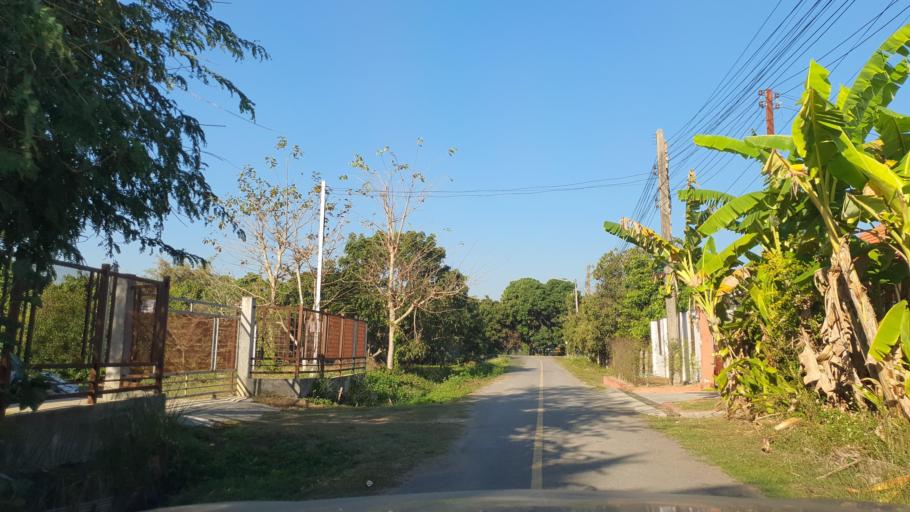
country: TH
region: Chiang Mai
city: Saraphi
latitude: 18.6910
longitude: 99.0757
